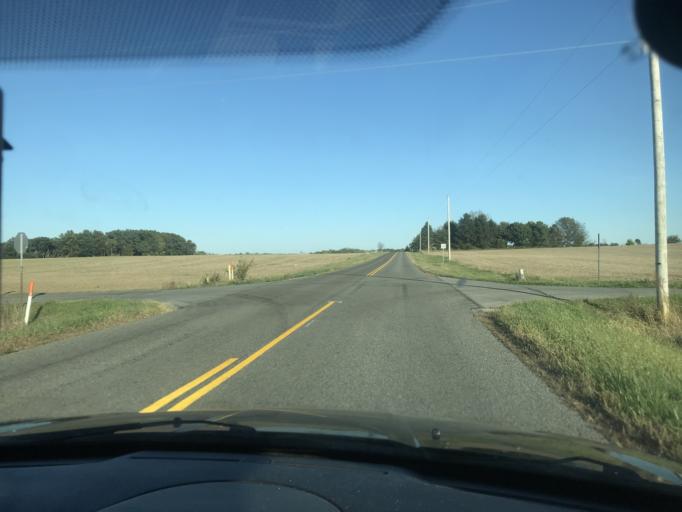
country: US
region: Ohio
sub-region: Logan County
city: Bellefontaine
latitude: 40.3202
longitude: -83.8066
